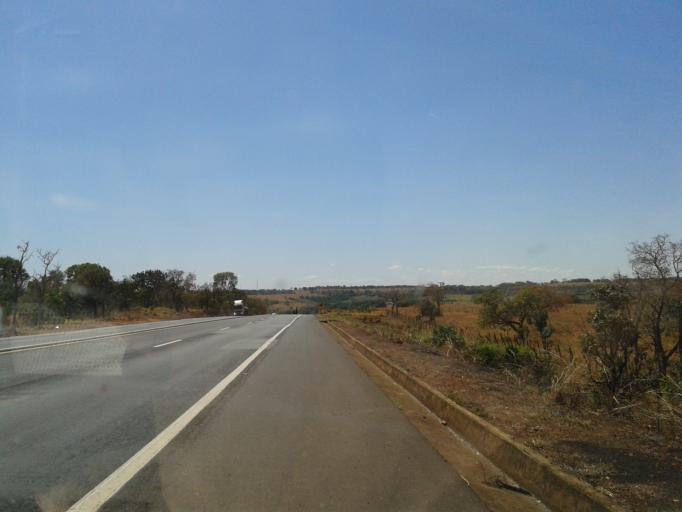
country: BR
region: Minas Gerais
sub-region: Monte Alegre De Minas
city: Monte Alegre de Minas
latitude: -18.8047
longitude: -49.0829
